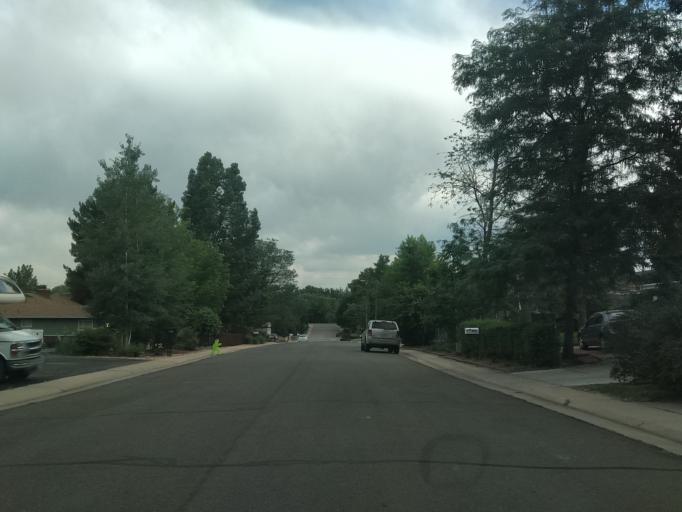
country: US
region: Colorado
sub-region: Jefferson County
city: Lakewood
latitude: 39.6992
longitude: -105.0991
